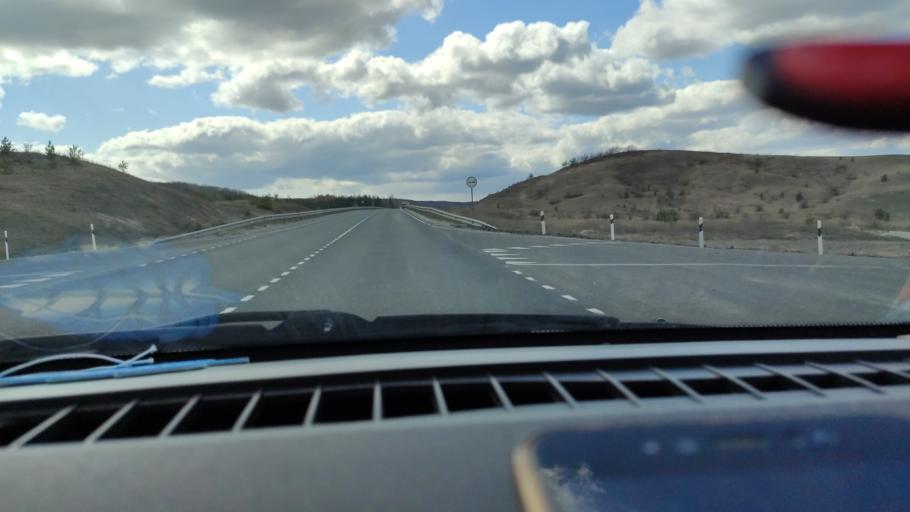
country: RU
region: Saratov
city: Alekseyevka
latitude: 52.3710
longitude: 47.9683
